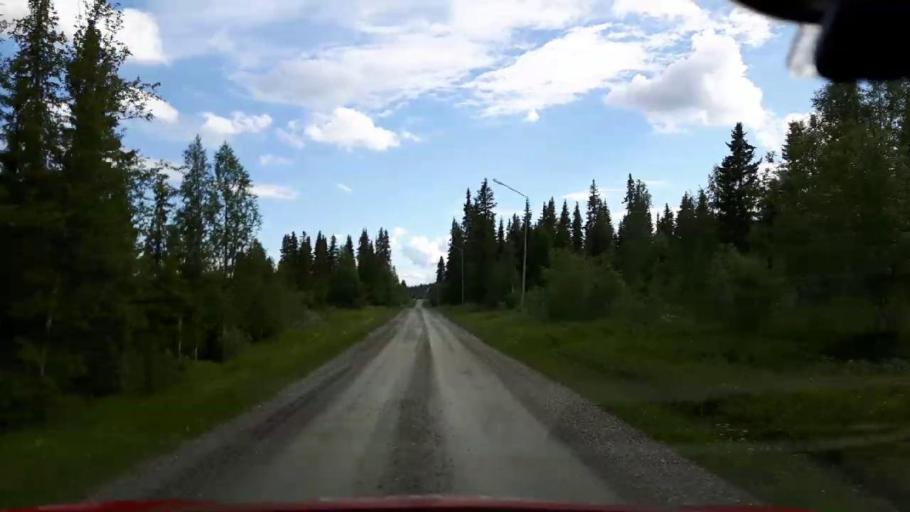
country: SE
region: Jaemtland
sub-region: Krokoms Kommun
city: Valla
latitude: 63.8337
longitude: 14.0401
